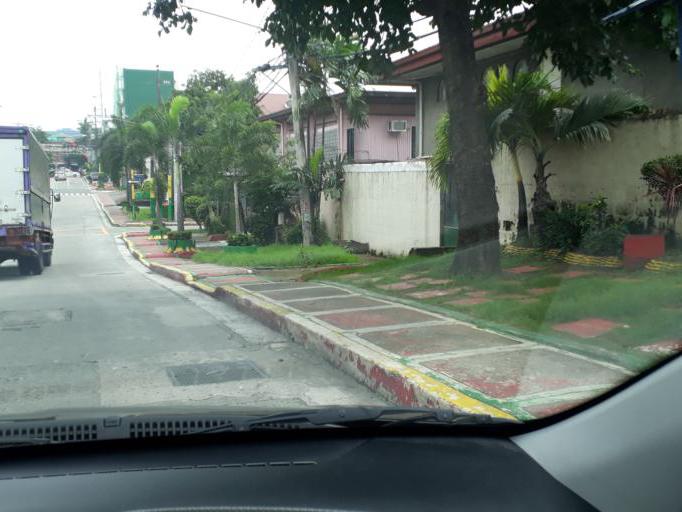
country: PH
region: Metro Manila
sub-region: Quezon City
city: Quezon City
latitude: 14.6304
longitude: 121.0503
